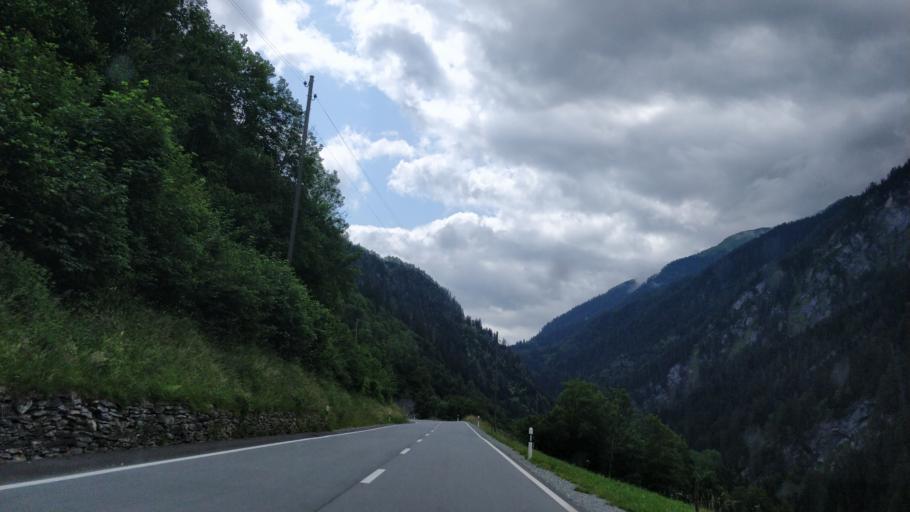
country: CH
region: Grisons
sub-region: Surselva District
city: Ilanz
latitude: 46.6826
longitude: 9.1805
